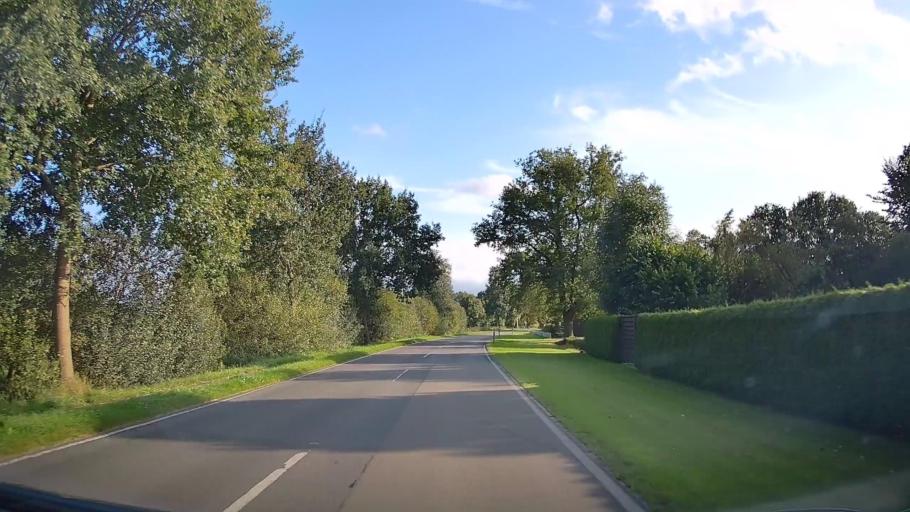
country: DE
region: Lower Saxony
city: Ostrhauderfehn
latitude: 53.1347
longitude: 7.6674
